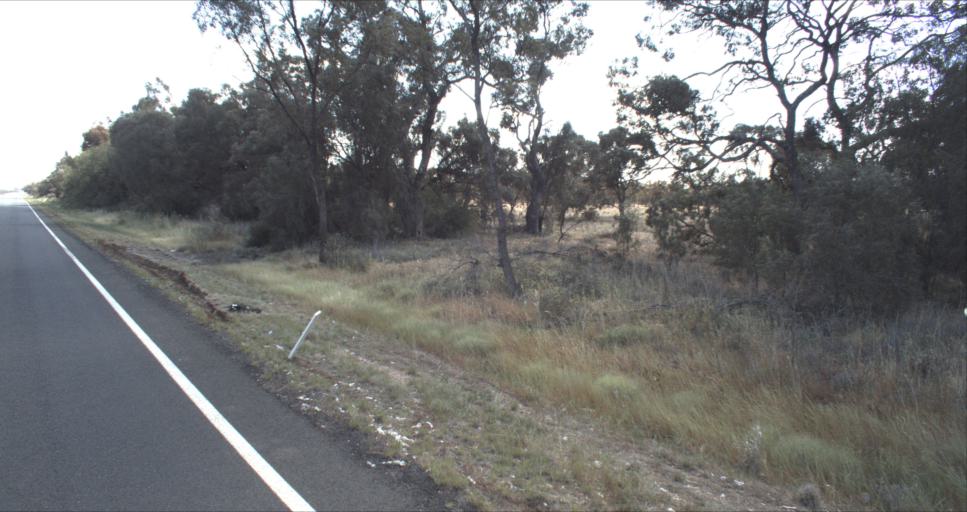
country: AU
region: New South Wales
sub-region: Murrumbidgee Shire
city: Darlington Point
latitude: -34.5315
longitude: 146.1738
